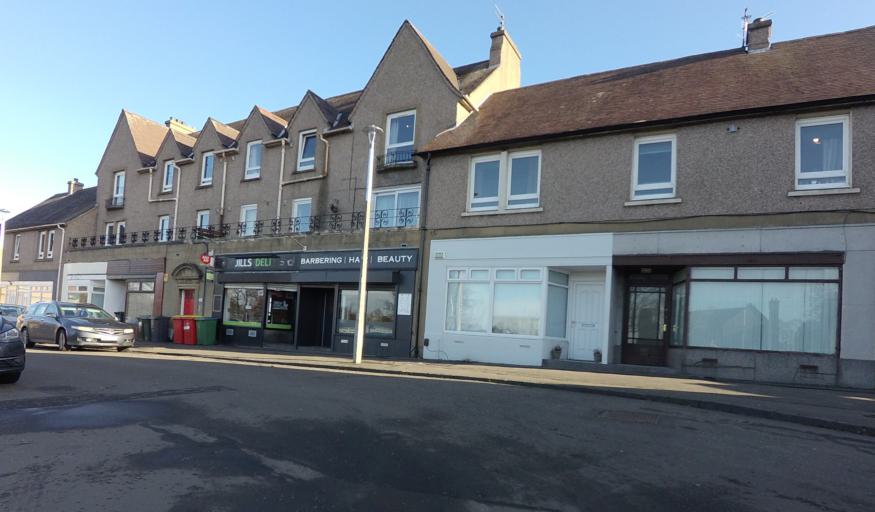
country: GB
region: Scotland
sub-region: Edinburgh
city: Colinton
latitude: 55.9595
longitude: -3.2889
